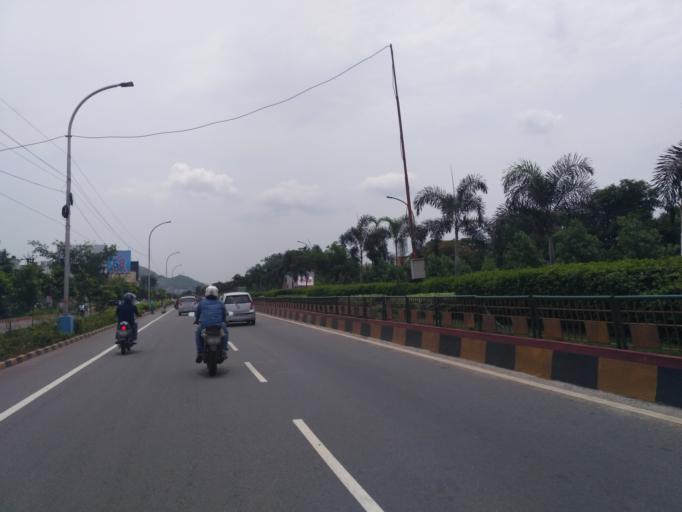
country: IN
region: Andhra Pradesh
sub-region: Vishakhapatnam
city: Vepagunta
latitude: 17.7465
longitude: 83.2508
